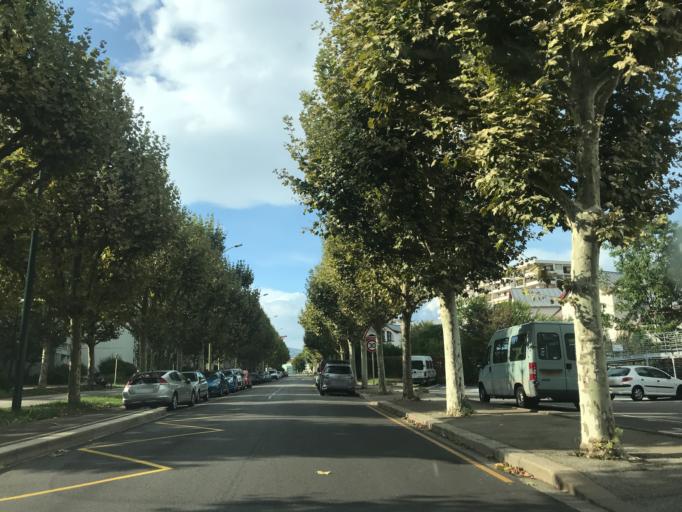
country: FR
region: Rhone-Alpes
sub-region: Departement de la Haute-Savoie
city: Annecy-le-Vieux
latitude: 45.9203
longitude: 6.1314
